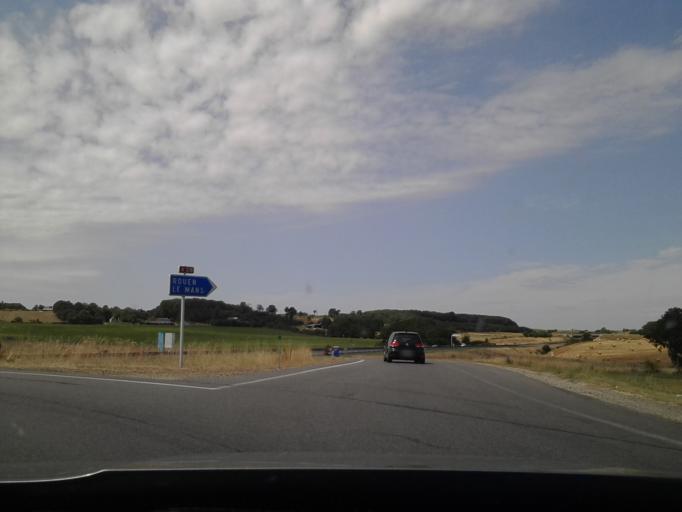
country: FR
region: Centre
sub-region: Departement d'Indre-et-Loire
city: Saint-Christophe-sur-le-Nais
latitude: 47.6502
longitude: 0.4677
